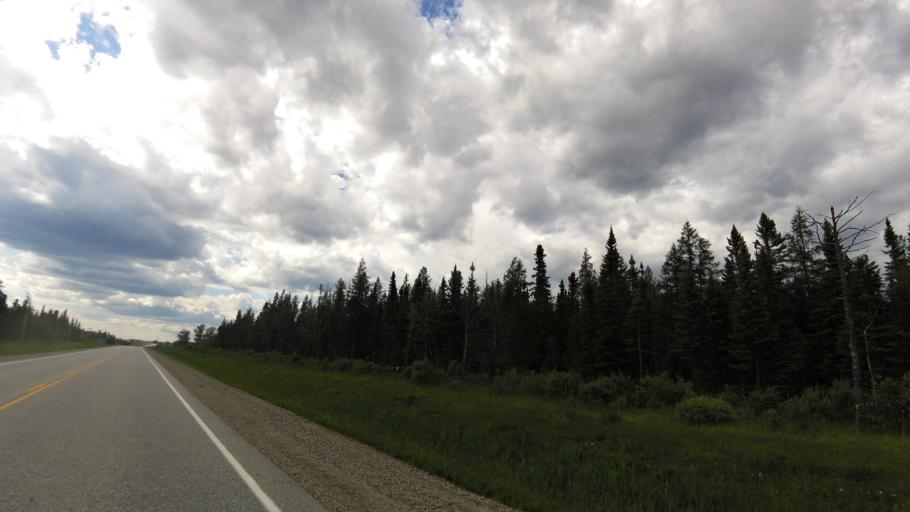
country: CA
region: Ontario
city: Hearst
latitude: 49.7053
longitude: -83.7694
